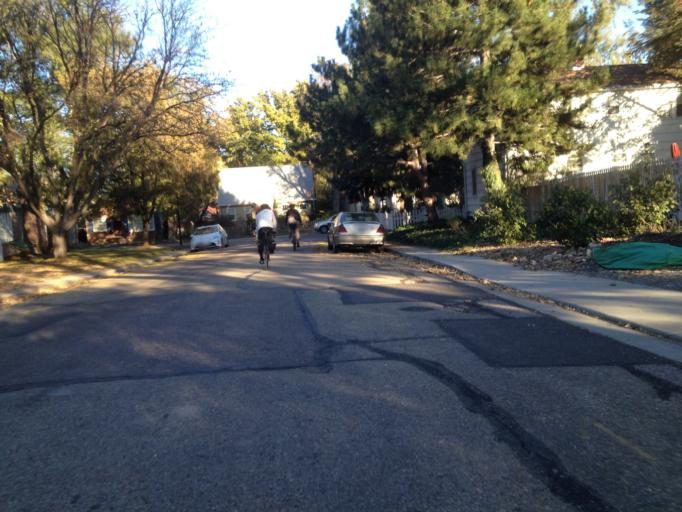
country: US
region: Colorado
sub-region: Boulder County
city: Longmont
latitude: 40.1716
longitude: -105.1125
